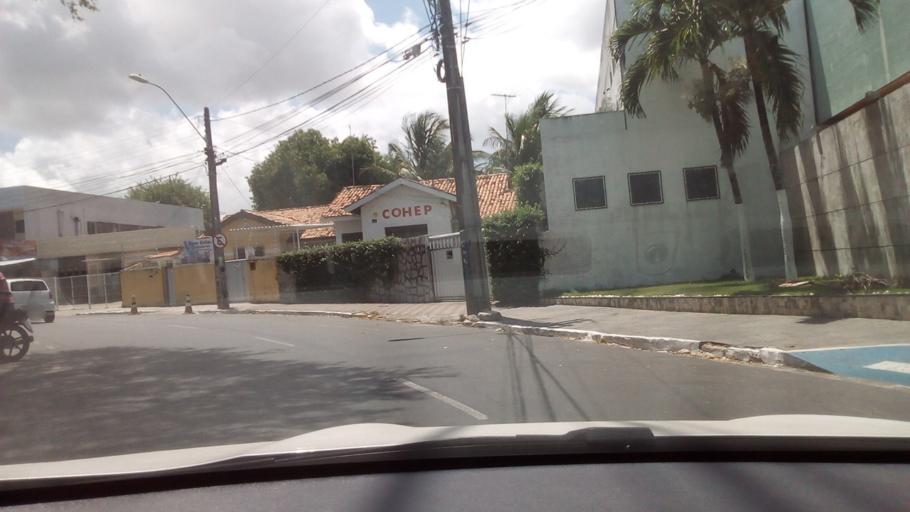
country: BR
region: Paraiba
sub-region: Joao Pessoa
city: Joao Pessoa
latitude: -7.1224
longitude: -34.8671
